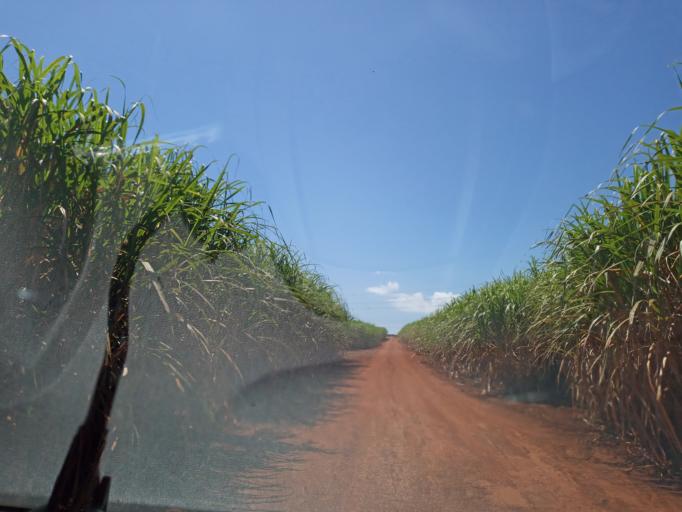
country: BR
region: Goias
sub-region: Itumbiara
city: Itumbiara
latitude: -18.4408
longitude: -49.1386
